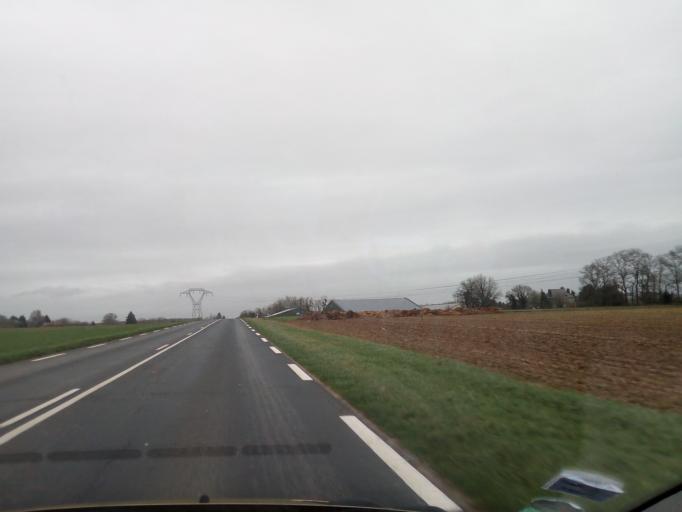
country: FR
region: Haute-Normandie
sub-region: Departement de l'Eure
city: Hauville
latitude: 49.3952
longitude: 0.7978
